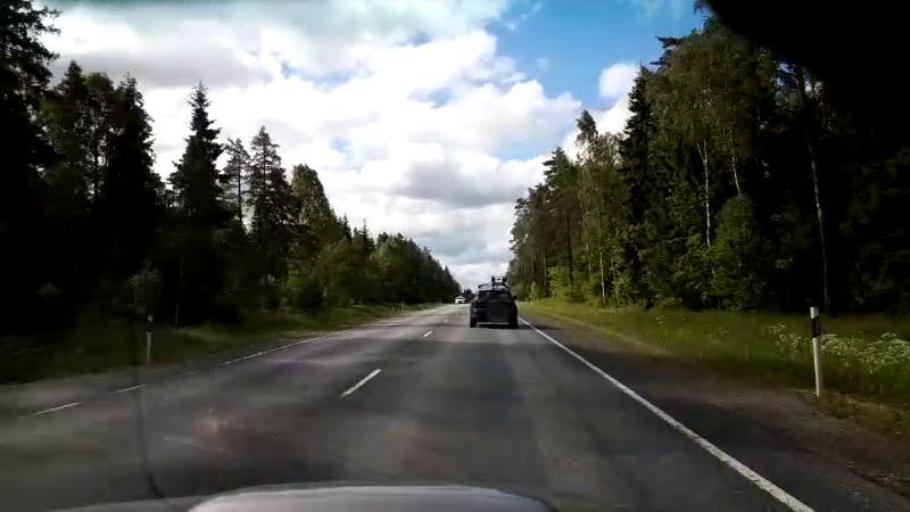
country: EE
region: Harju
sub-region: Saue linn
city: Saue
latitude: 59.1975
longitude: 24.4985
